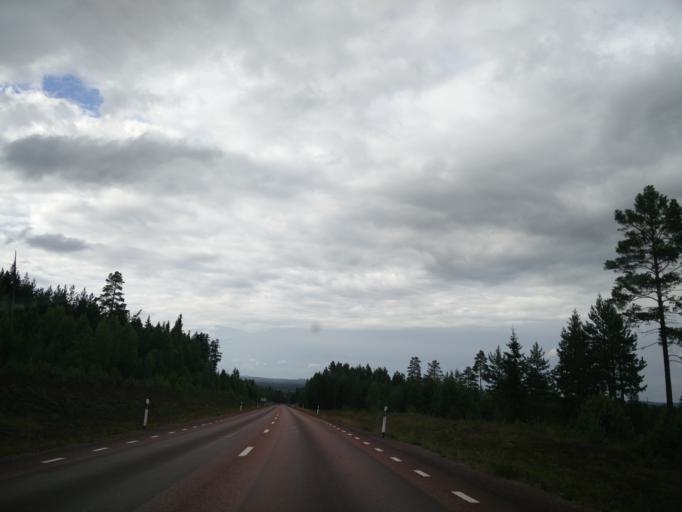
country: SE
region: Dalarna
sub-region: Malung-Saelens kommun
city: Malung
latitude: 60.6667
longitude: 13.7013
